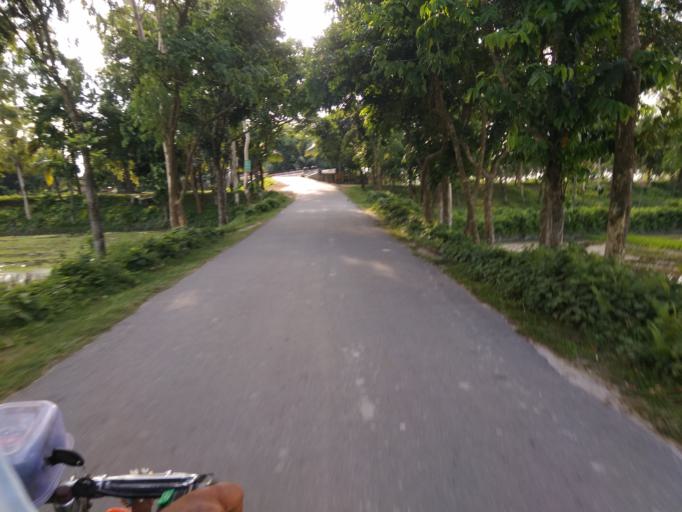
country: BD
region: Rangpur Division
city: Rangpur
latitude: 25.8322
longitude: 89.1140
